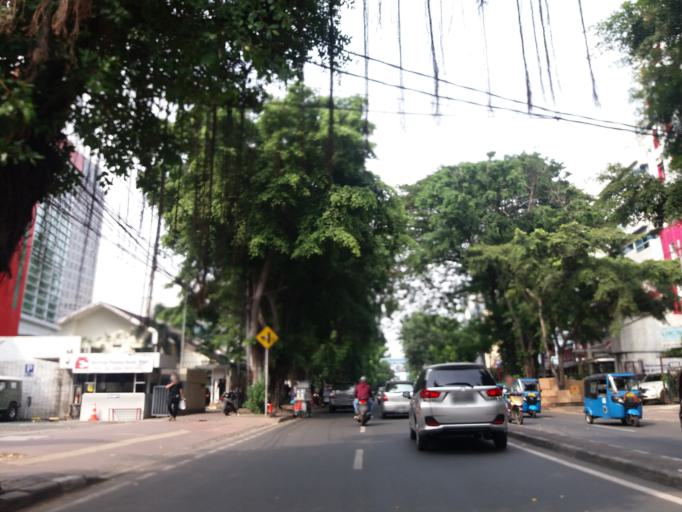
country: ID
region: Jakarta Raya
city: Jakarta
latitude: -6.1870
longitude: 106.8203
